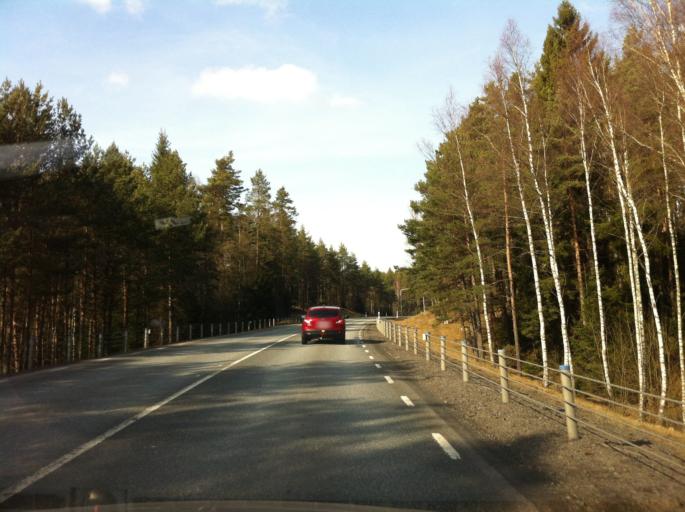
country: SE
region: Joenkoeping
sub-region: Mullsjo Kommun
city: Mullsjoe
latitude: 57.9820
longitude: 13.8309
